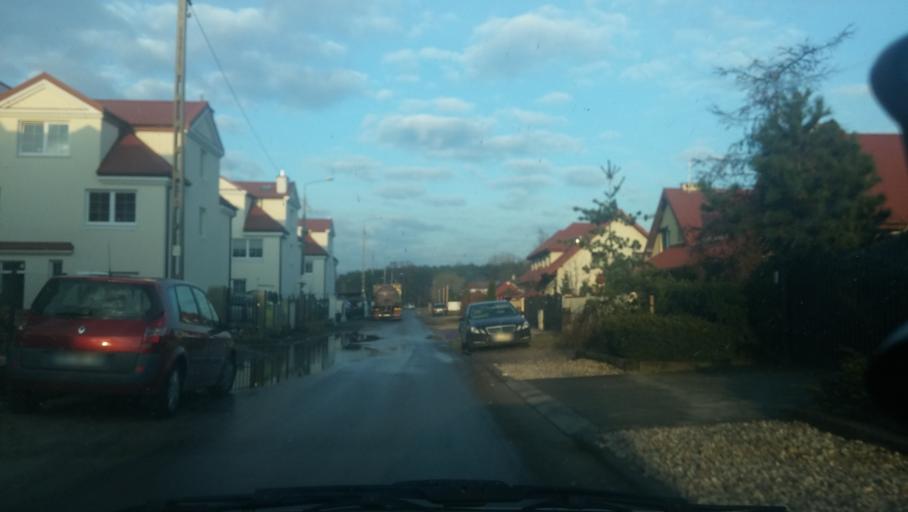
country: PL
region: Masovian Voivodeship
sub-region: Warszawa
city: Wawer
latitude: 52.1955
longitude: 21.1484
